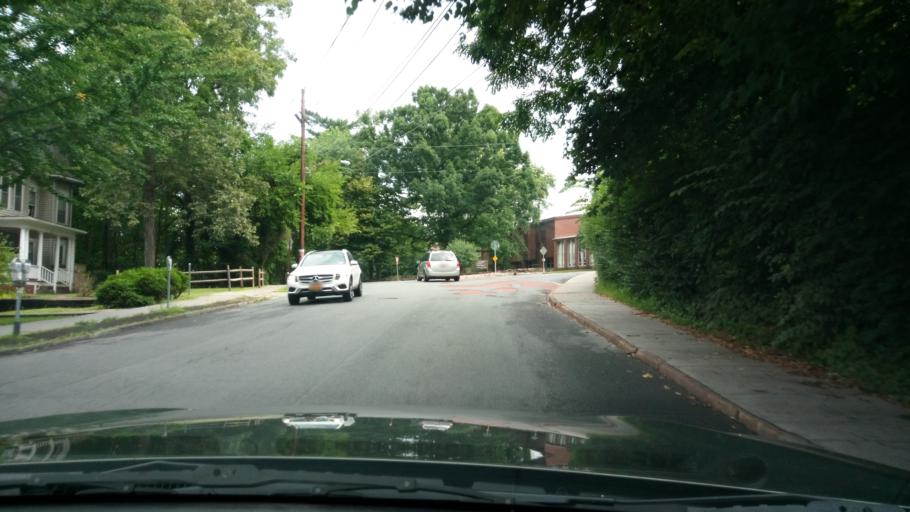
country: US
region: New York
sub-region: Tompkins County
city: Ithaca
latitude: 42.4445
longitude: -76.4894
